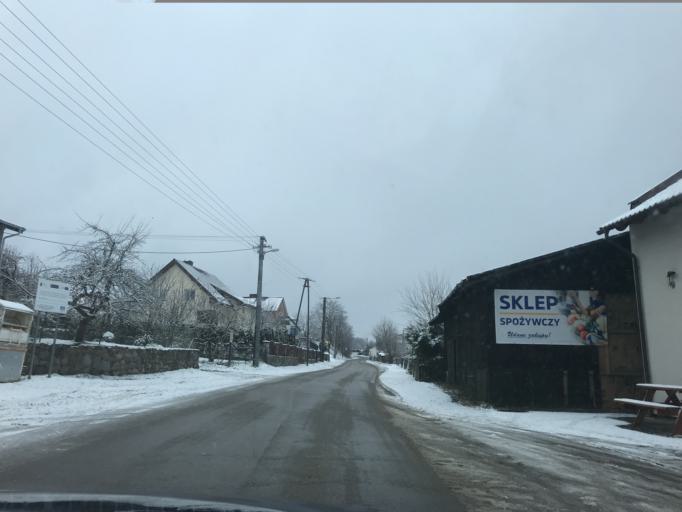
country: PL
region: Pomeranian Voivodeship
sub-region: Powiat bytowski
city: Bytow
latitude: 54.2168
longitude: 17.5615
